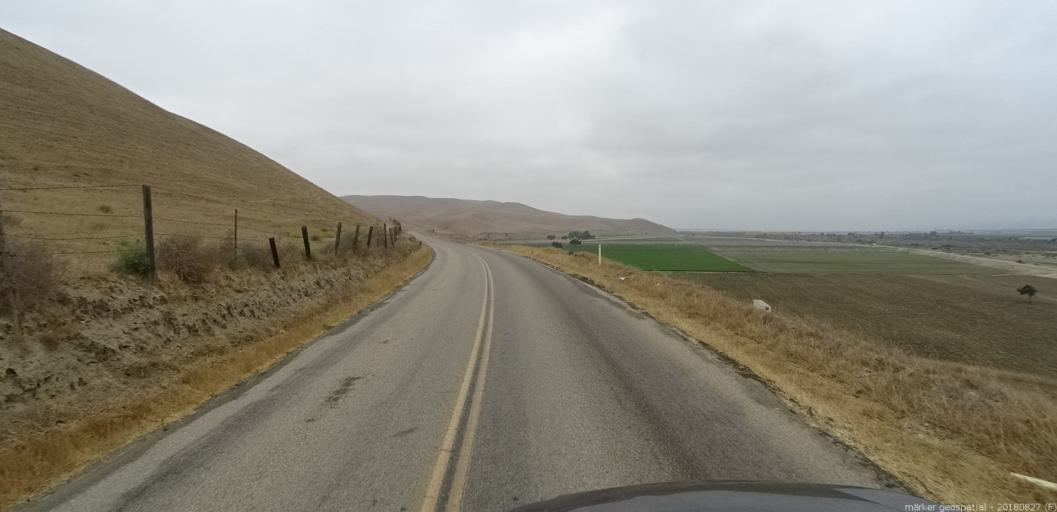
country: US
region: California
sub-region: Monterey County
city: Greenfield
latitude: 36.3378
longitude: -121.1981
